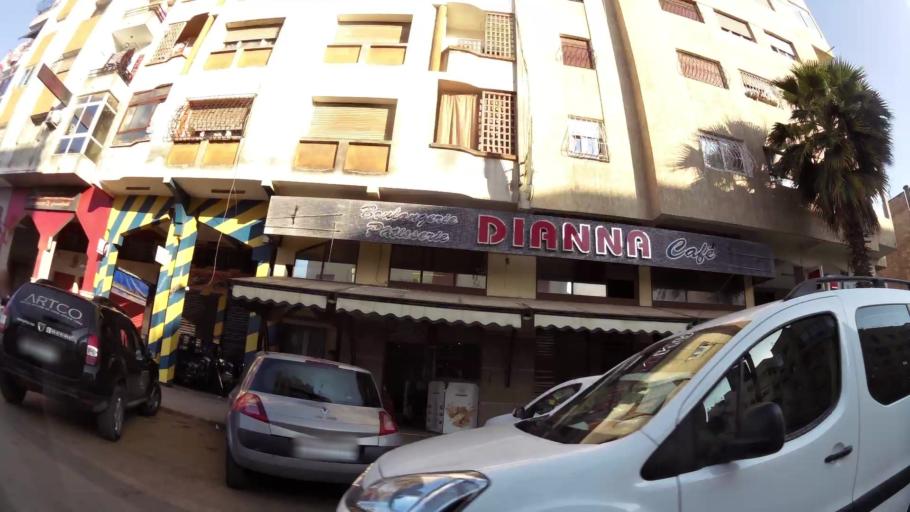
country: MA
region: Rabat-Sale-Zemmour-Zaer
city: Sale
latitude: 34.0557
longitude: -6.7922
